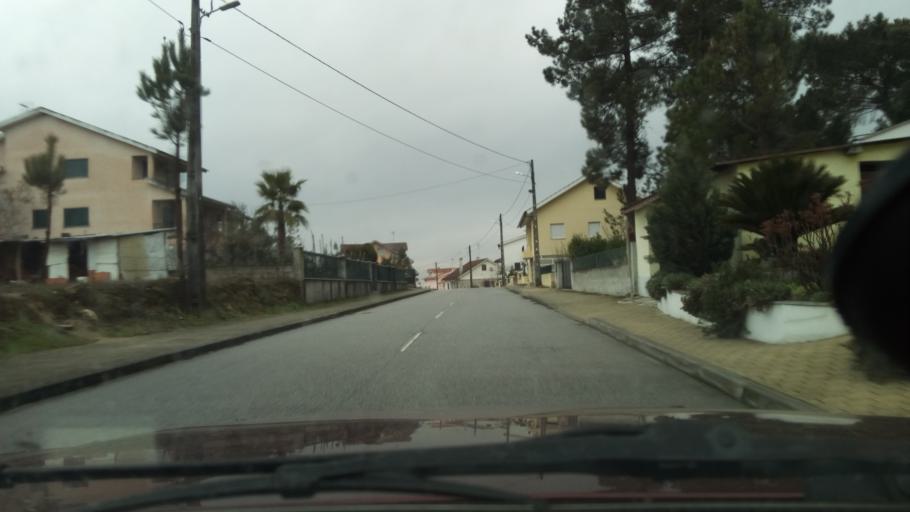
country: PT
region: Viseu
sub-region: Mangualde
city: Mangualde
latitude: 40.6170
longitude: -7.7965
